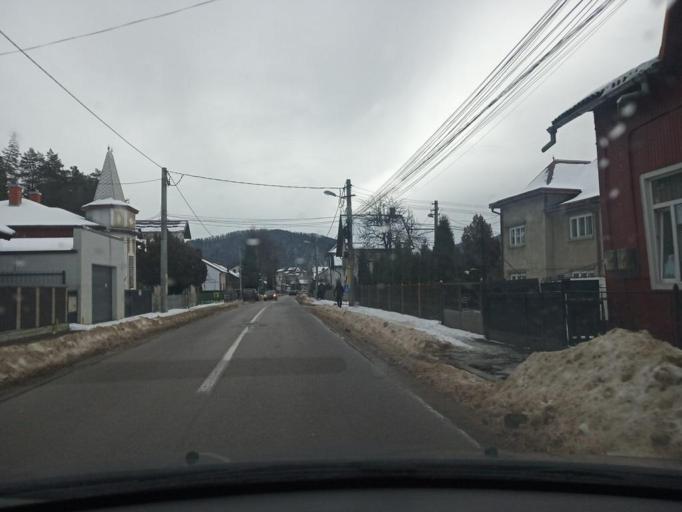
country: RO
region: Suceava
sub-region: Oras Gura Humorului
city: Gura Humorului
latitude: 47.5589
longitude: 25.8888
